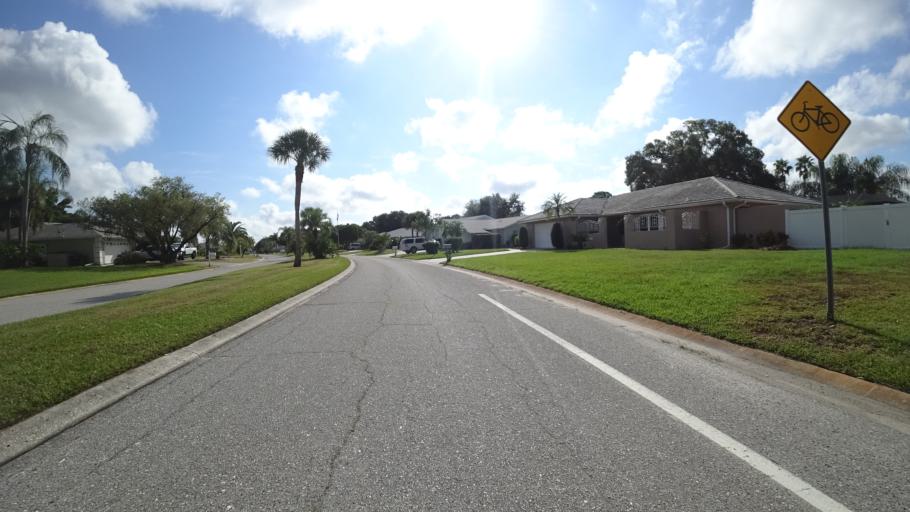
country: US
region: Florida
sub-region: Sarasota County
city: Desoto Lakes
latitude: 27.3996
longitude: -82.4964
